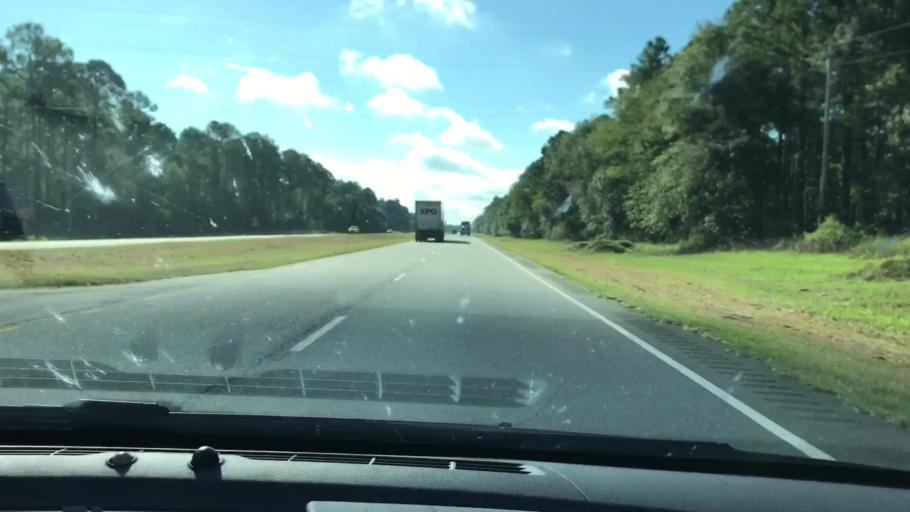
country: US
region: Georgia
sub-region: Dougherty County
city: Albany
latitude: 31.5663
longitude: -84.0182
